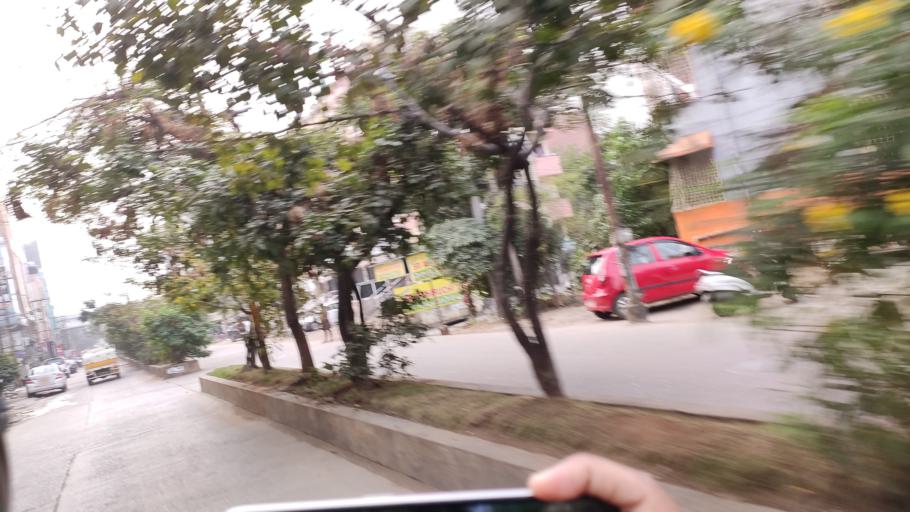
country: IN
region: Telangana
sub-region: Rangareddi
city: Kukatpalli
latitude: 17.4862
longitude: 78.3888
